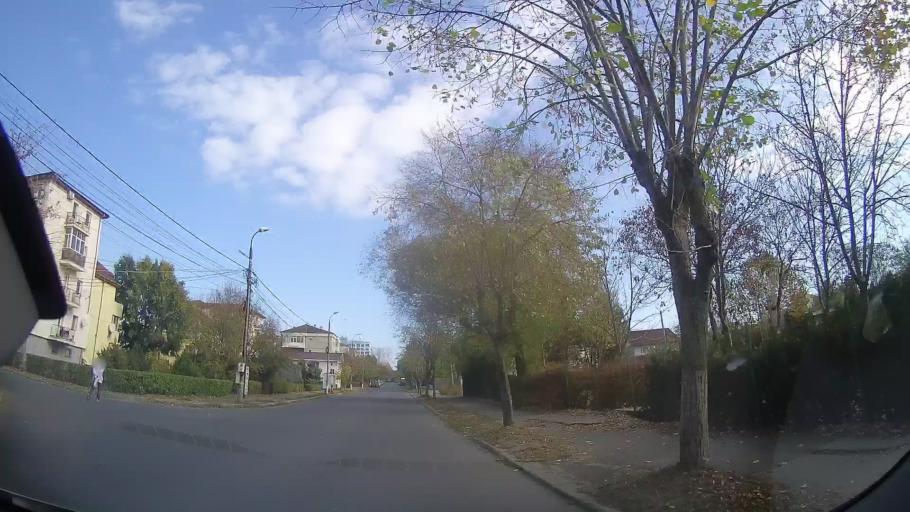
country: RO
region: Constanta
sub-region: Oras Eforie
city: Eforie Nord
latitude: 44.0606
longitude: 28.6279
